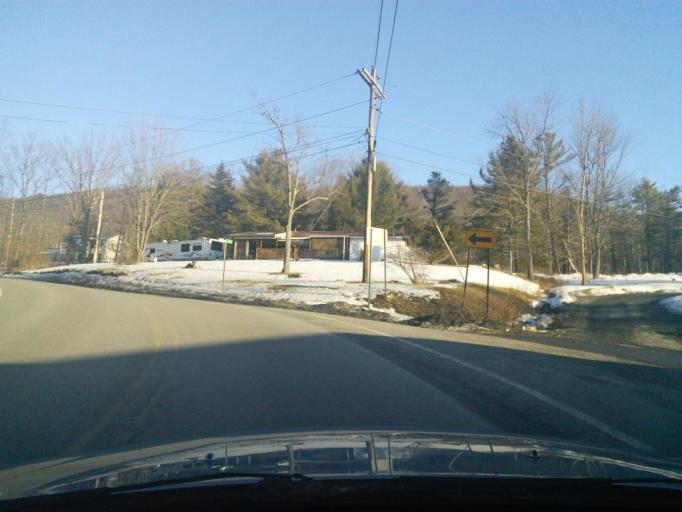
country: US
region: Pennsylvania
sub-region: Centre County
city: Park Forest Village
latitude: 40.8615
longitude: -77.9364
